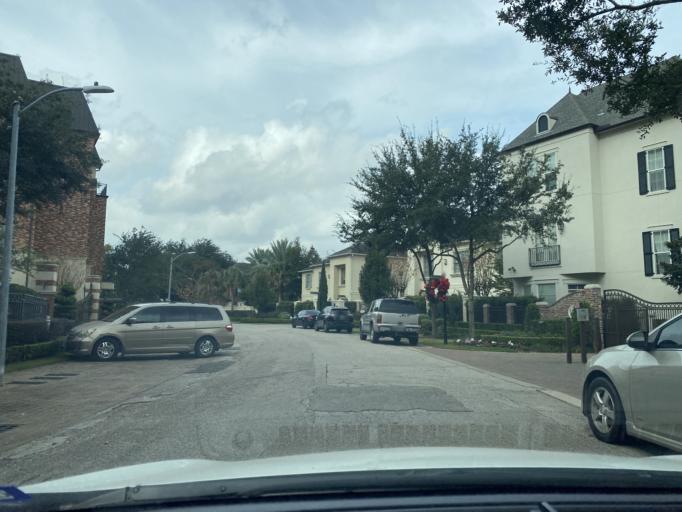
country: US
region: Texas
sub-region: Harris County
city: Hunters Creek Village
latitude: 29.7550
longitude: -95.4607
